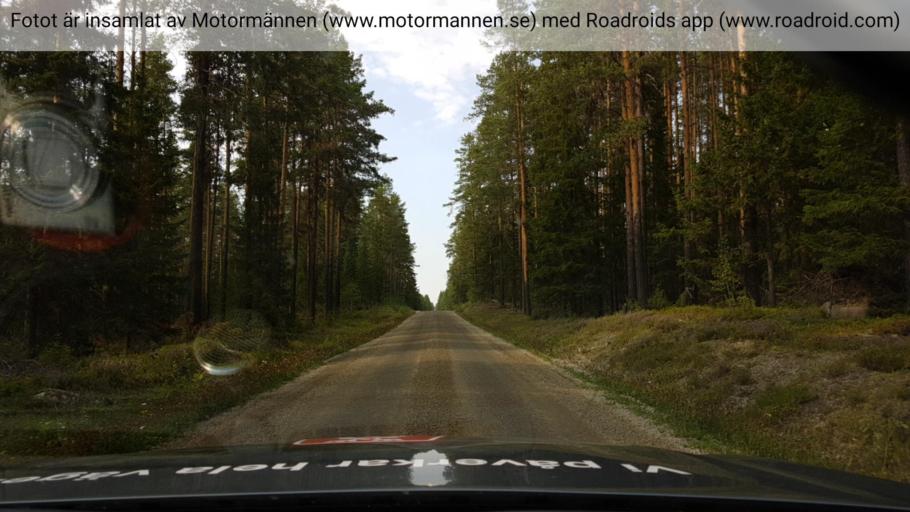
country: SE
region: Jaemtland
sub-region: Braecke Kommun
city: Braecke
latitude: 62.4949
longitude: 14.9222
